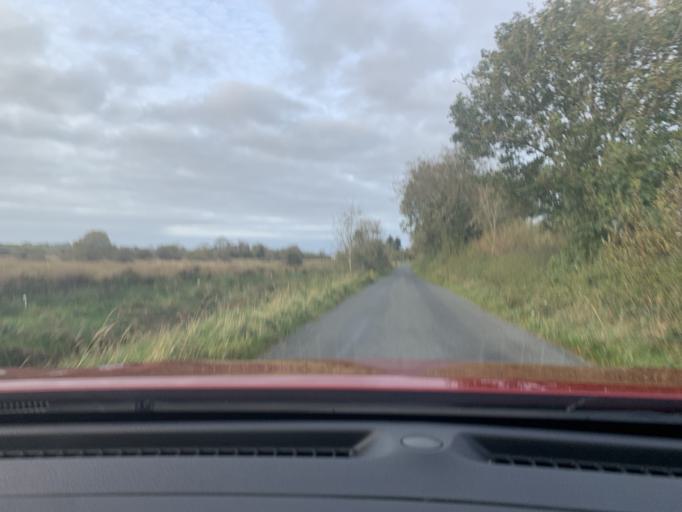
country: IE
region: Connaught
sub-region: Roscommon
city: Ballaghaderreen
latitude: 53.9958
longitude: -8.6081
